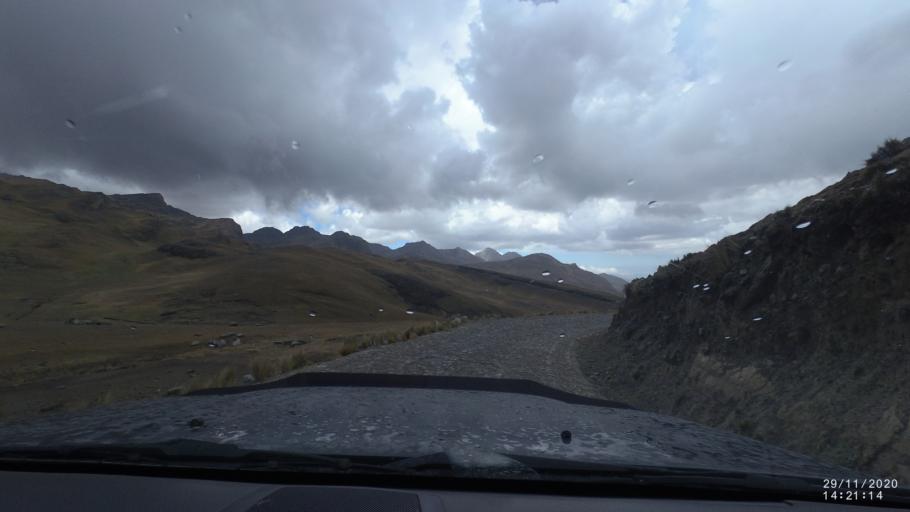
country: BO
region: Cochabamba
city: Sipe Sipe
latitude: -17.2500
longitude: -66.3889
